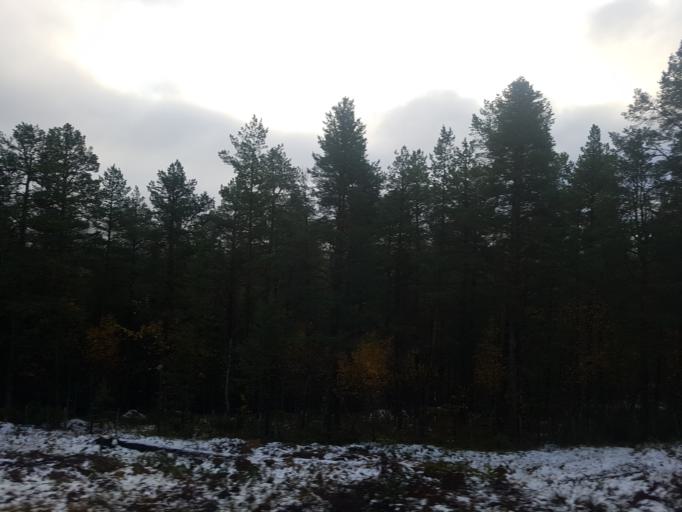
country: NO
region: Sor-Trondelag
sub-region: Oppdal
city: Oppdal
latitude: 62.6369
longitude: 9.8038
